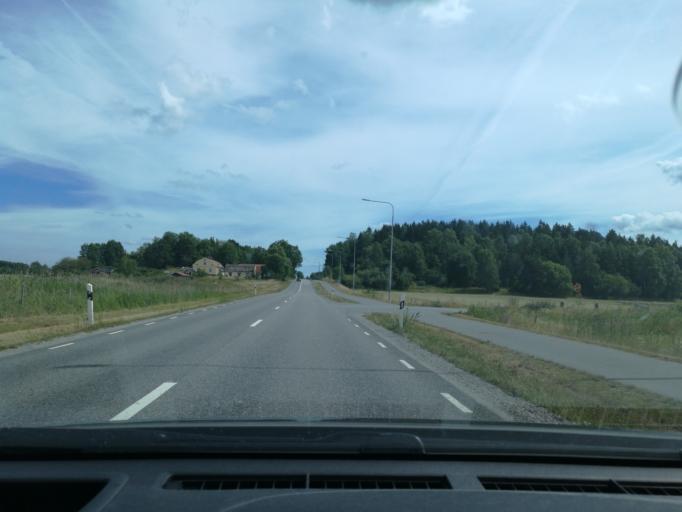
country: SE
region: Stockholm
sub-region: Sigtuna Kommun
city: Marsta
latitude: 59.6092
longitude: 17.8719
